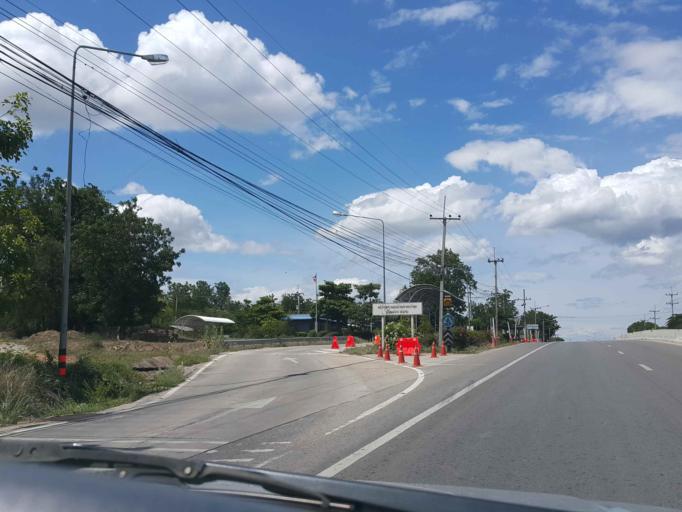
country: TH
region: Chiang Mai
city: Doi Lo
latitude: 18.4626
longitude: 98.7804
